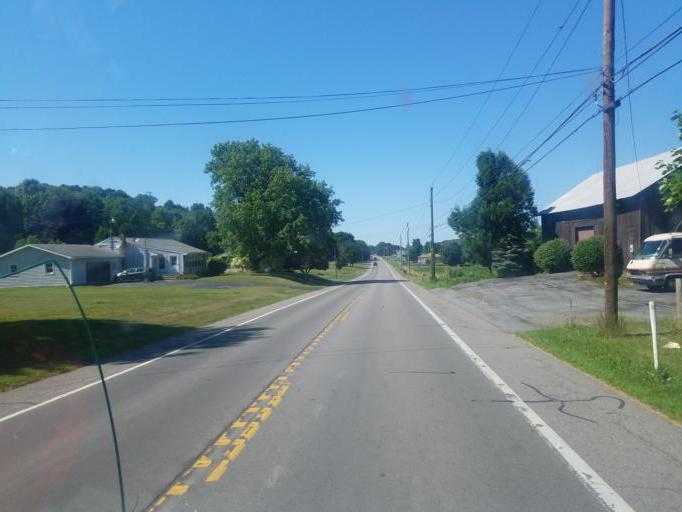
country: US
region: New York
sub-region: Wayne County
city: Newark
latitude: 43.0156
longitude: -77.0938
